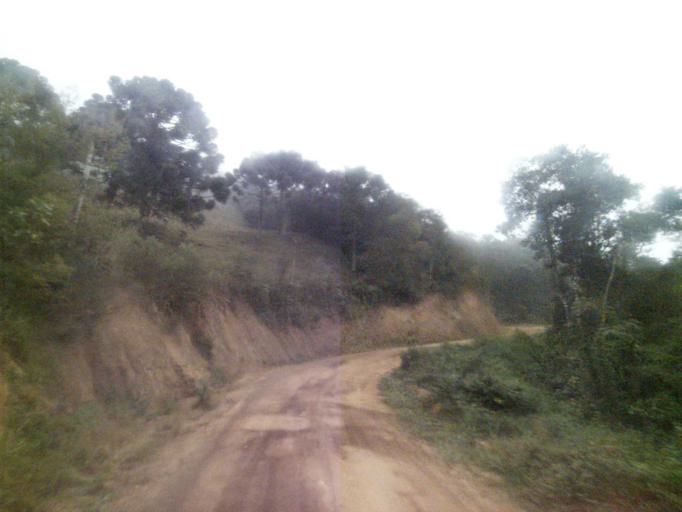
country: BR
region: Santa Catarina
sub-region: Anitapolis
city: Anitapolis
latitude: -27.8551
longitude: -49.1345
